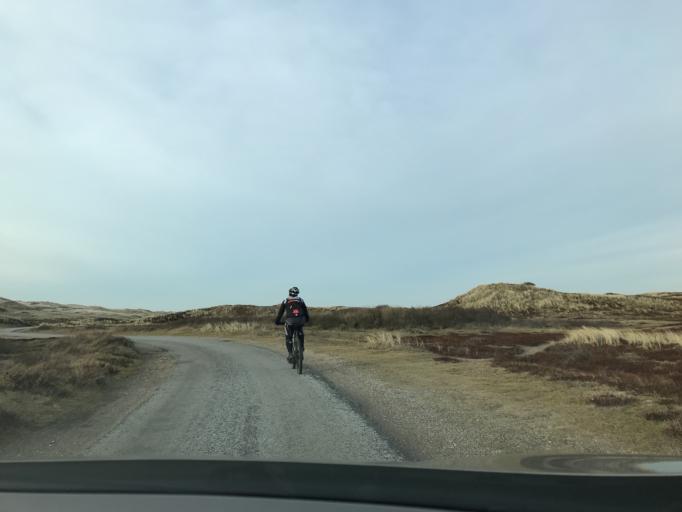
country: DK
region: Central Jutland
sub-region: Ringkobing-Skjern Kommune
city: Hvide Sande
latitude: 55.8127
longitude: 8.1773
